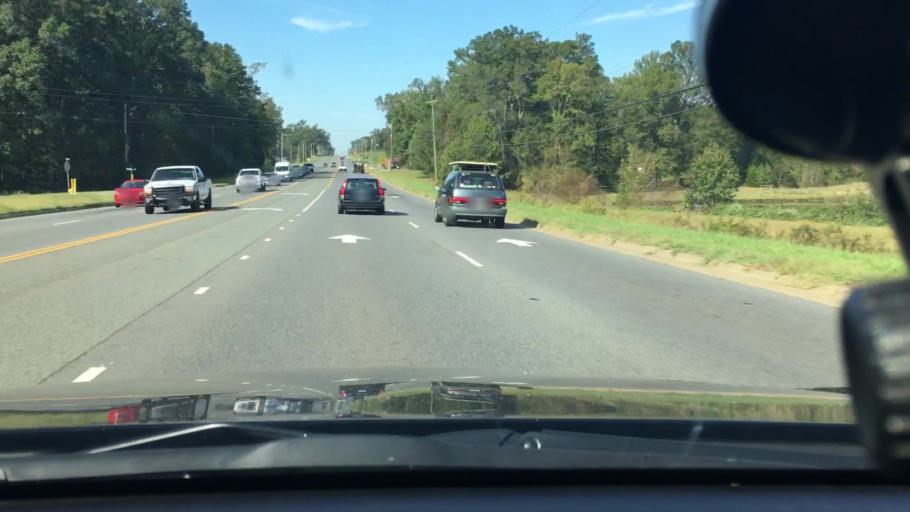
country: US
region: North Carolina
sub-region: Cabarrus County
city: Midland
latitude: 35.2497
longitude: -80.5288
